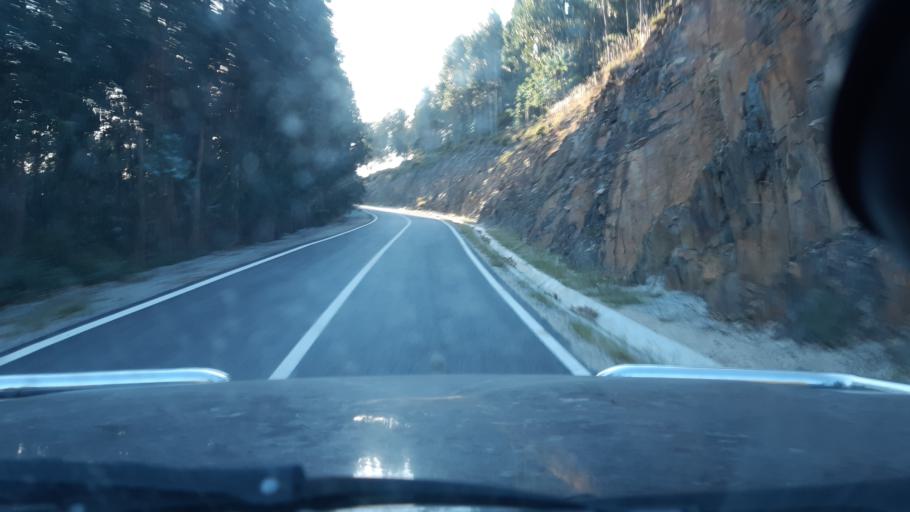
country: PT
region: Viseu
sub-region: Mortagua
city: Mortagua
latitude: 40.5402
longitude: -8.2472
